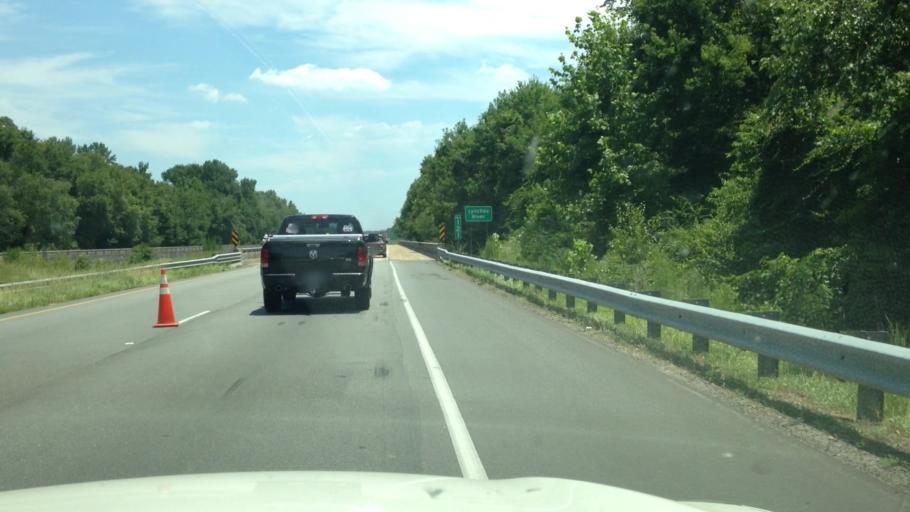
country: US
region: South Carolina
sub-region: Lee County
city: Bishopville
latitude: 34.1874
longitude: -80.1951
